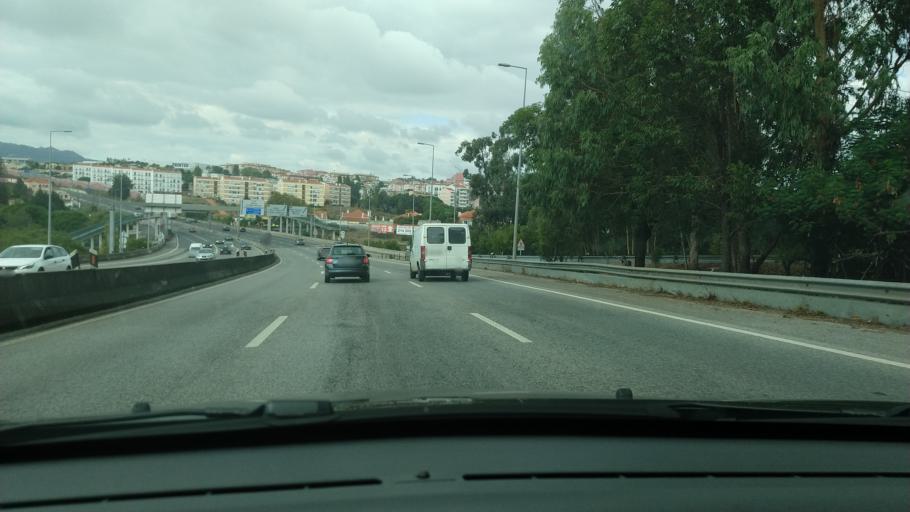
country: PT
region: Lisbon
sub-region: Sintra
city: Rio de Mouro
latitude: 38.7772
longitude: -9.3234
